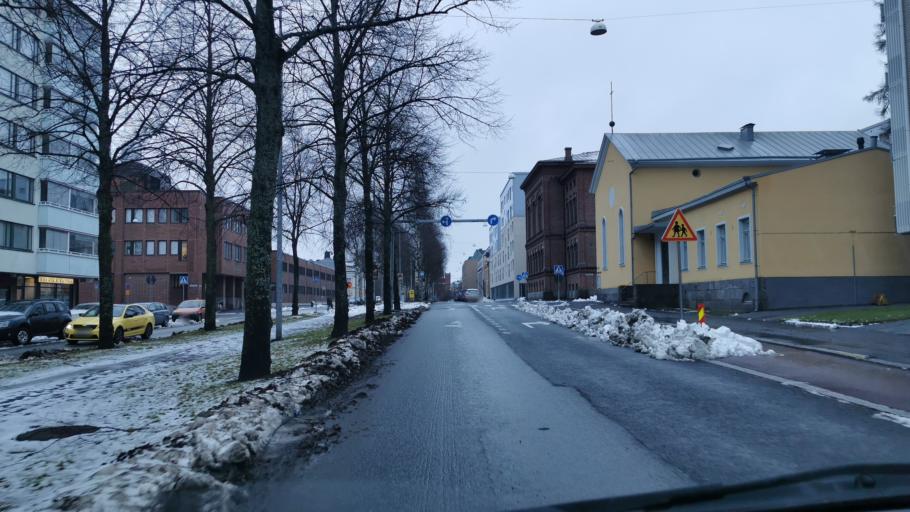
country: FI
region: Ostrobothnia
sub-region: Vaasa
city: Vaasa
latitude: 63.0988
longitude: 21.6064
